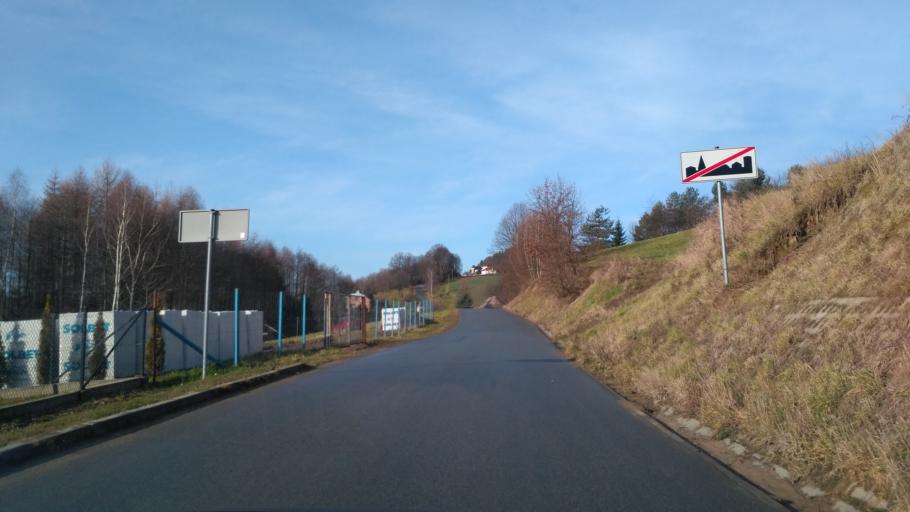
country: PL
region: Subcarpathian Voivodeship
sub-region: Powiat krosnienski
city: Korczyna
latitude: 49.7229
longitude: 21.8041
